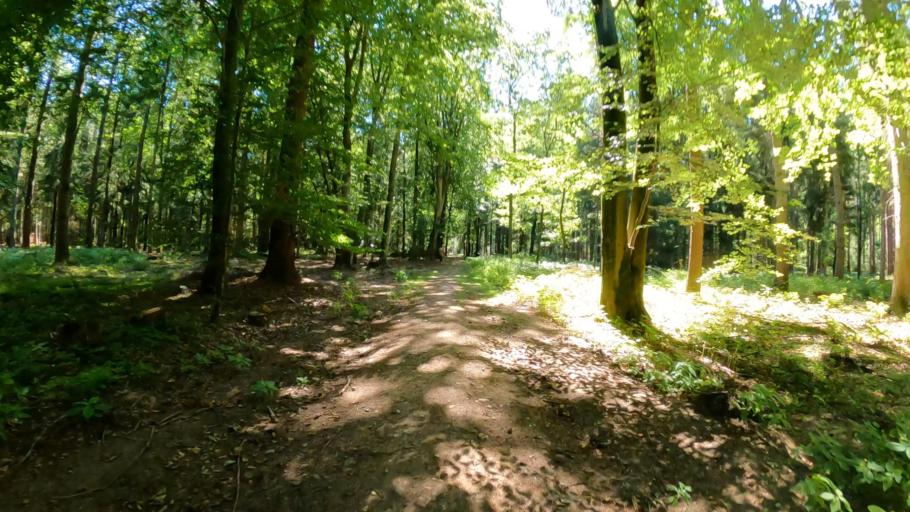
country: DE
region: Schleswig-Holstein
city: Kroppelshagen-Fahrendorf
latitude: 53.4815
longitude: 10.3441
